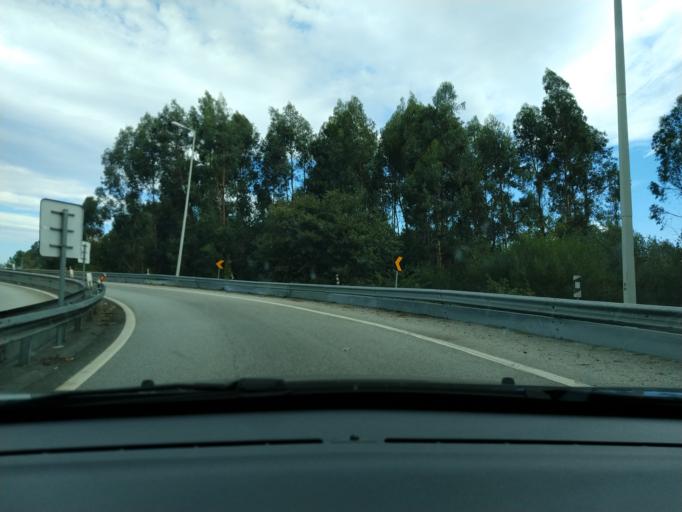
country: PT
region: Aveiro
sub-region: Albergaria-A-Velha
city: Albergaria-a-Velha
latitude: 40.6847
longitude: -8.5242
